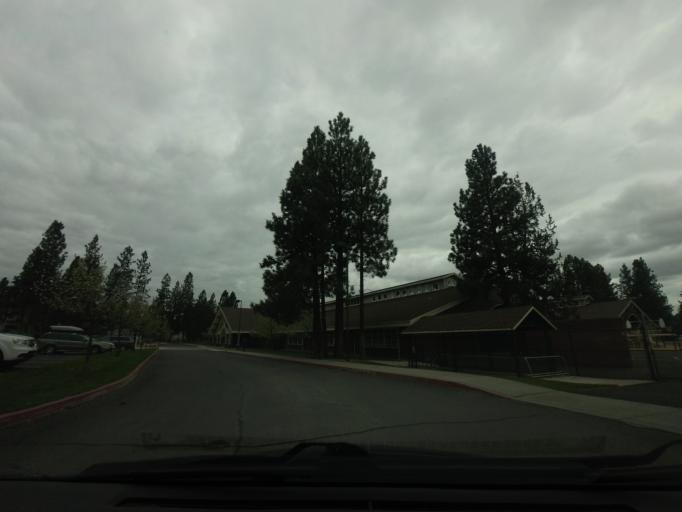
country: US
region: Oregon
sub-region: Deschutes County
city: Bend
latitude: 44.0235
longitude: -121.3306
